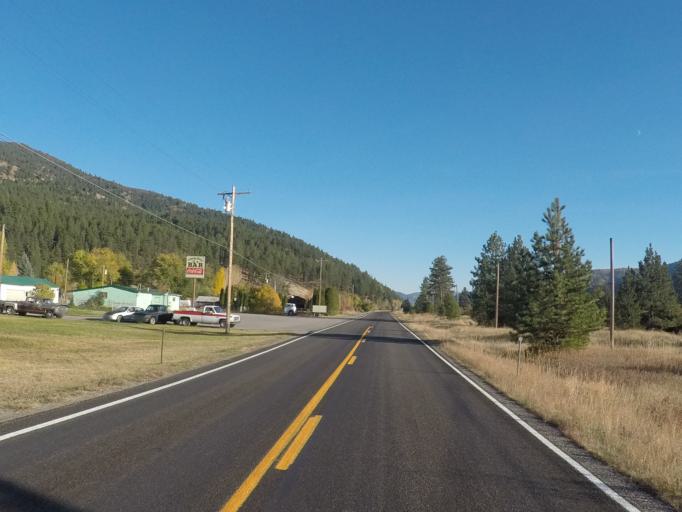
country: US
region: Montana
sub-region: Missoula County
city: Bonner-West Riverside
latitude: 46.8356
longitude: -113.8258
